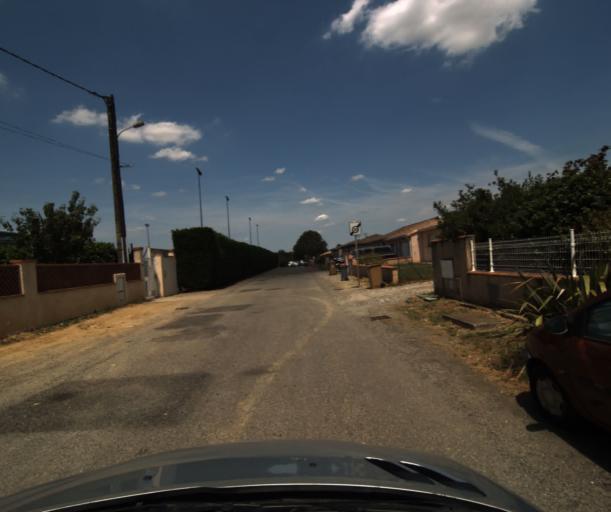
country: FR
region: Midi-Pyrenees
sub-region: Departement de la Haute-Garonne
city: Saint-Lys
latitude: 43.5142
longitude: 1.1863
